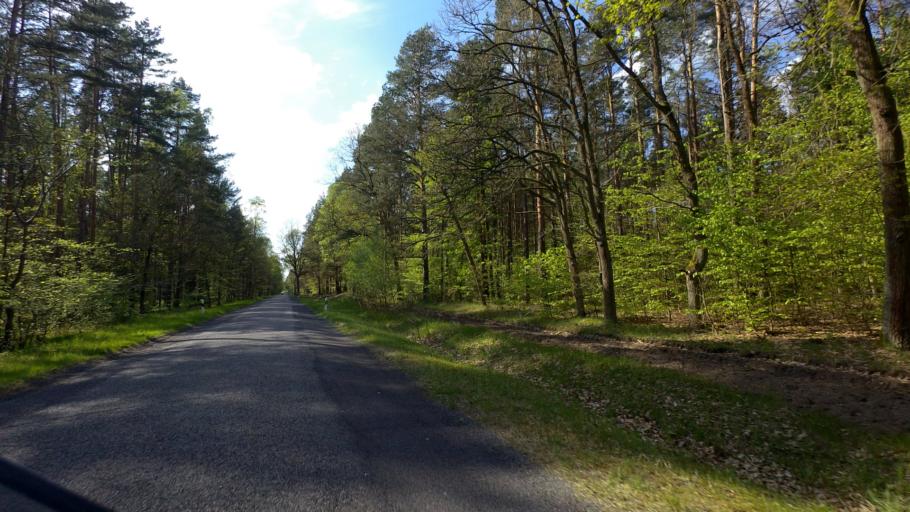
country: DE
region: Brandenburg
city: Zehdenick
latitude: 53.0142
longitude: 13.4219
